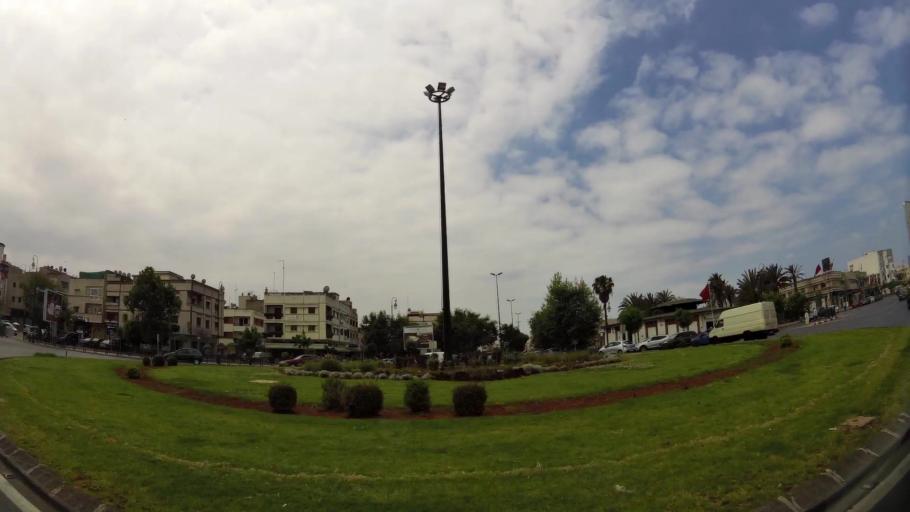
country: MA
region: Rabat-Sale-Zemmour-Zaer
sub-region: Skhirate-Temara
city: Temara
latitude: 33.9768
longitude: -6.8869
